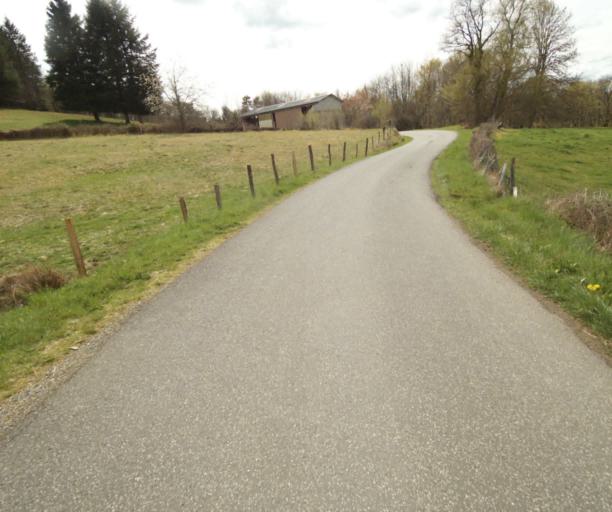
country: FR
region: Limousin
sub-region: Departement de la Correze
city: Laguenne
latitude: 45.2182
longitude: 1.8670
